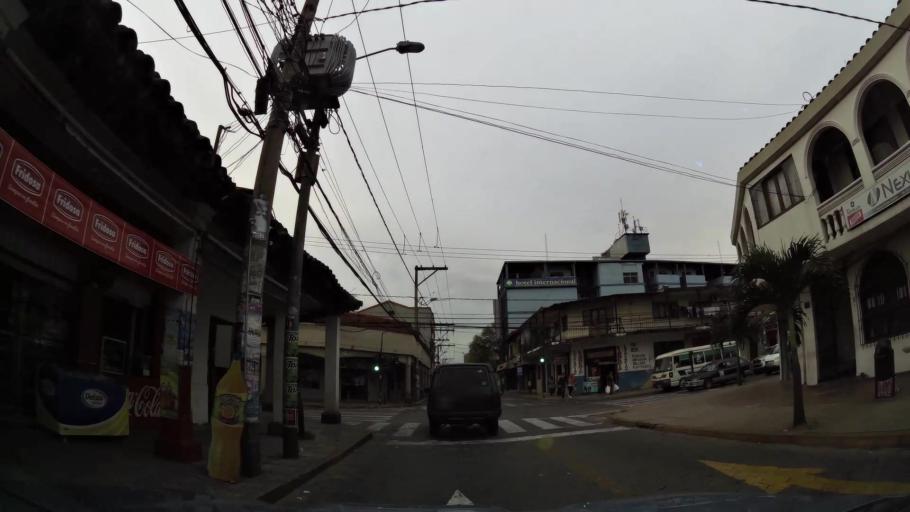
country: BO
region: Santa Cruz
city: Santa Cruz de la Sierra
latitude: -17.7884
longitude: -63.1842
